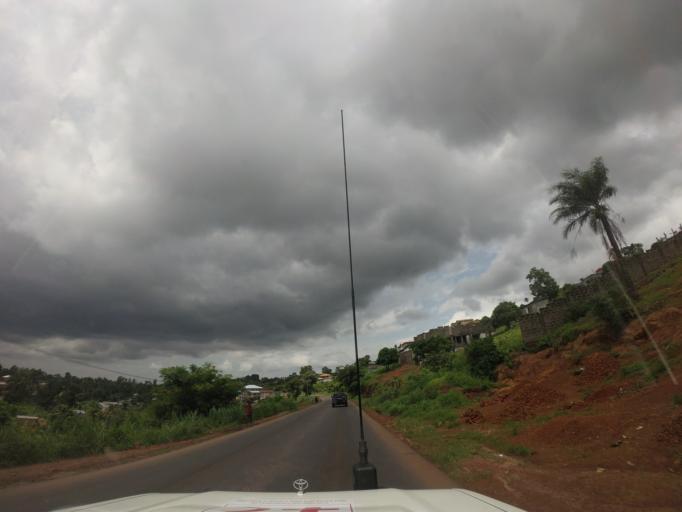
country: SL
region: Western Area
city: Waterloo
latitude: 8.3439
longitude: -13.0749
